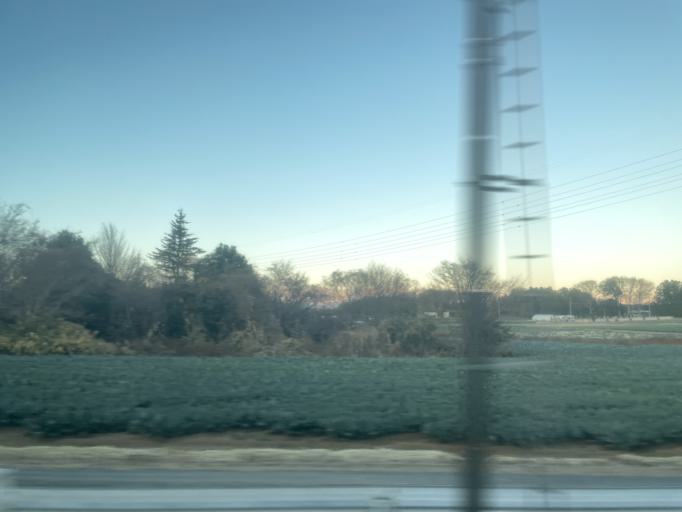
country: JP
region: Saitama
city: Honjo
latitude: 36.2144
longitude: 139.2224
